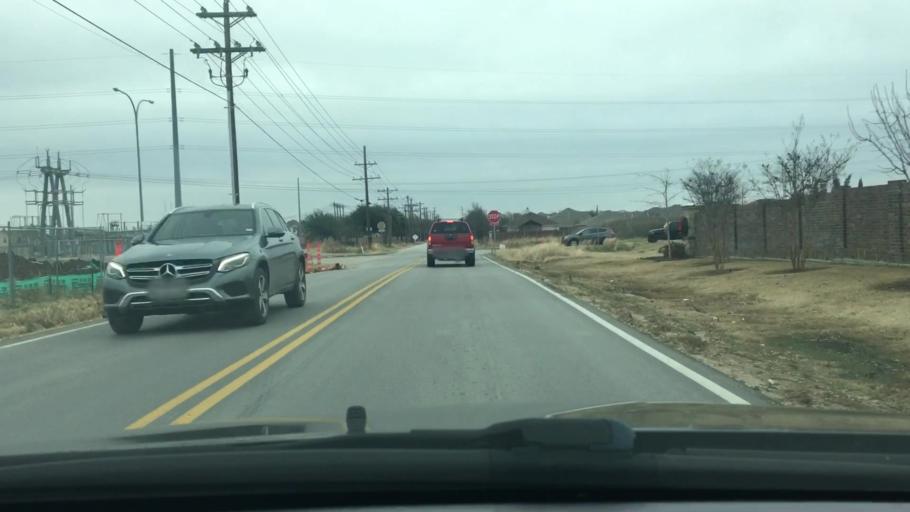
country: US
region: Texas
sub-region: Tarrant County
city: Keller
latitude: 32.9637
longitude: -97.2652
